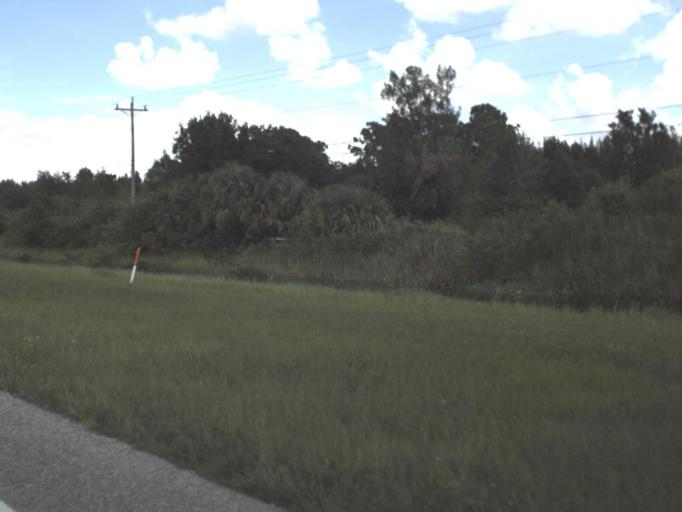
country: US
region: Florida
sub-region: Lee County
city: Burnt Store Marina
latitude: 26.7932
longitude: -81.9460
